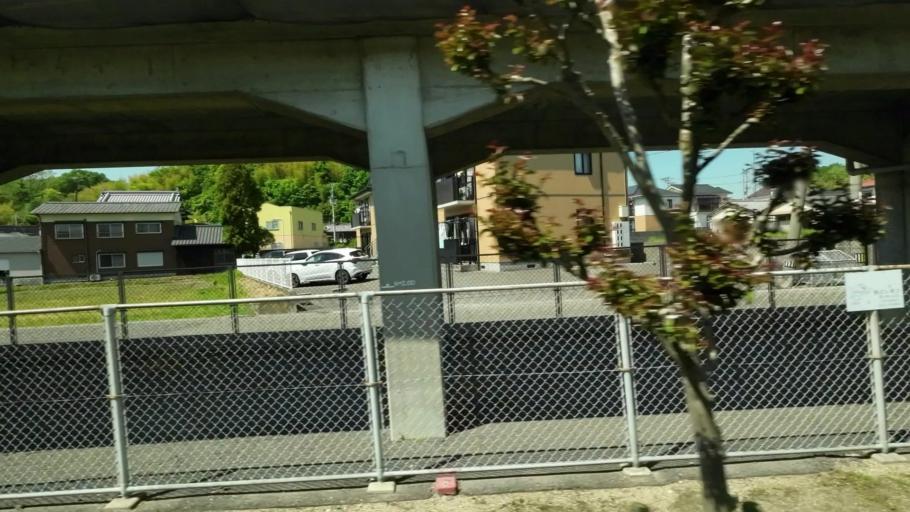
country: JP
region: Ehime
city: Hojo
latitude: 34.0722
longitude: 132.9870
